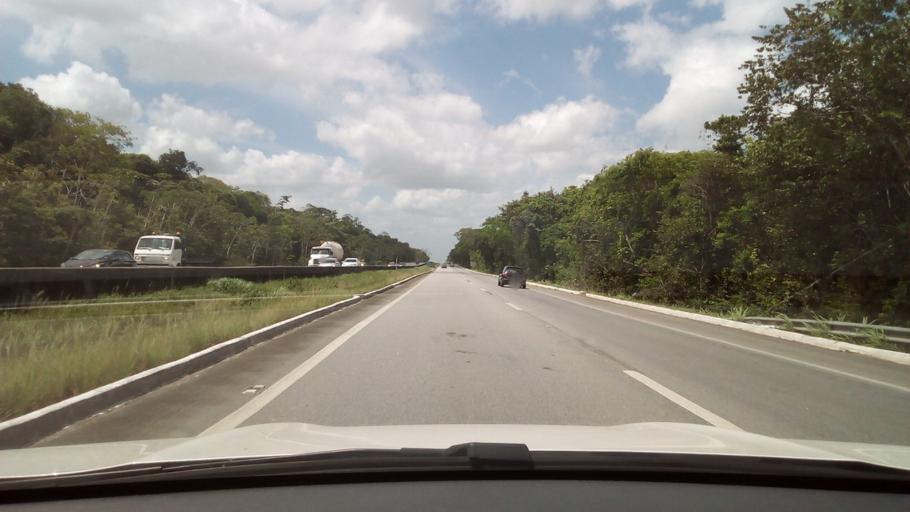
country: BR
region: Paraiba
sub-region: Mamanguape
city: Mamanguape
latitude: -6.9793
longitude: -35.0769
